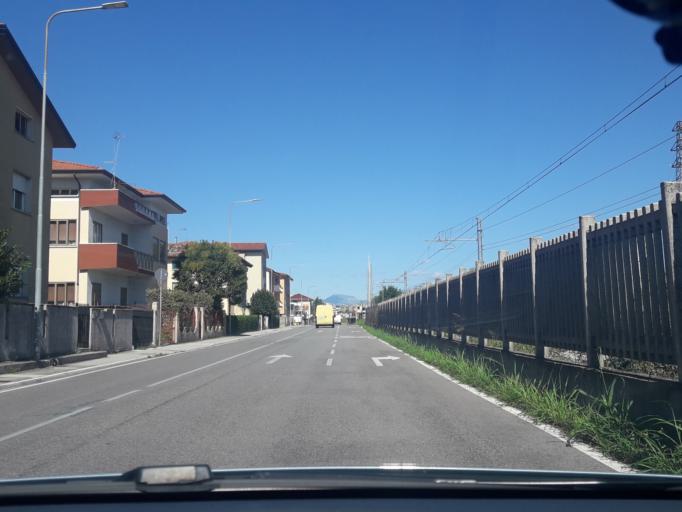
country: IT
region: Friuli Venezia Giulia
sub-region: Provincia di Udine
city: Basaldella
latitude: 46.0415
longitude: 13.2332
